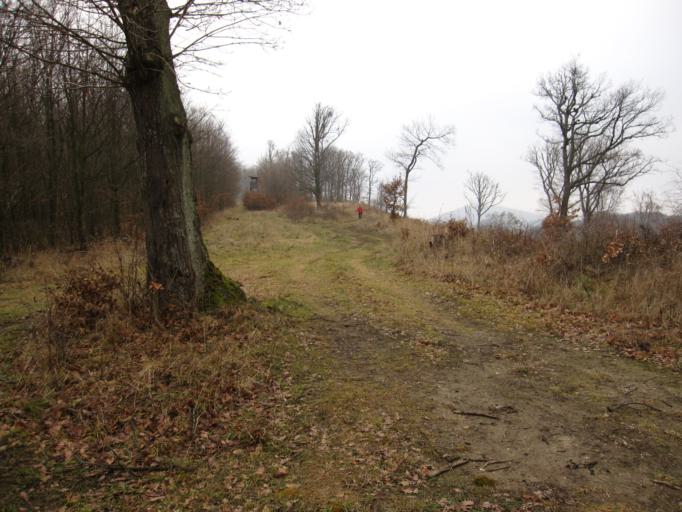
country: HU
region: Pest
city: Visegrad
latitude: 47.7246
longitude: 18.9754
